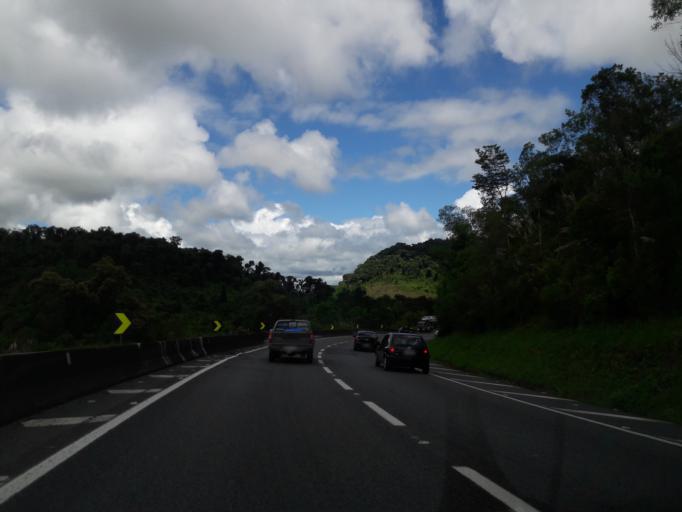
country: BR
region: Parana
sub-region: Antonina
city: Antonina
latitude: -25.0243
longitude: -48.5181
